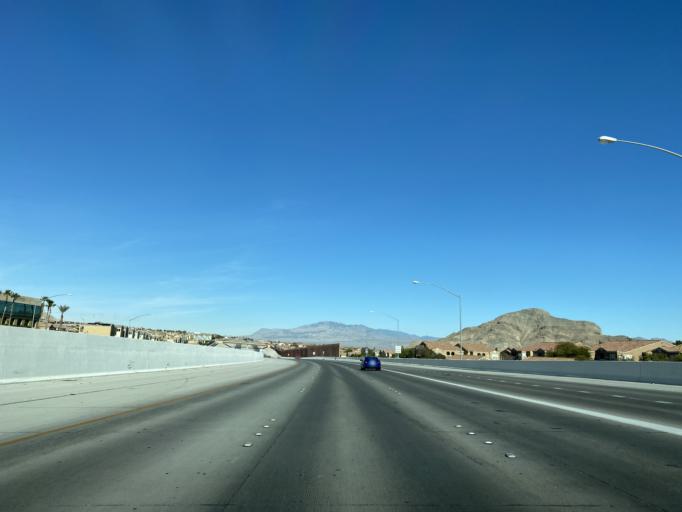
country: US
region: Nevada
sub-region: Clark County
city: Summerlin South
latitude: 36.2234
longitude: -115.3256
